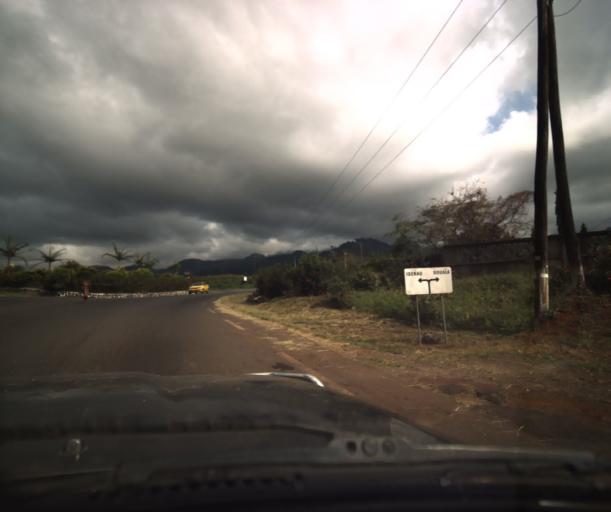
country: CM
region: South-West Province
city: Limbe
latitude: 4.0198
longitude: 9.1812
